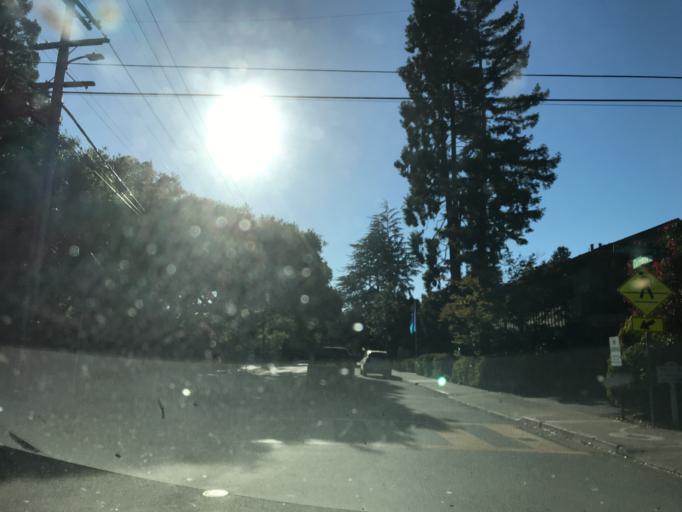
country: US
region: California
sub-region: San Mateo County
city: Menlo Park
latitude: 37.4624
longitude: -122.1632
